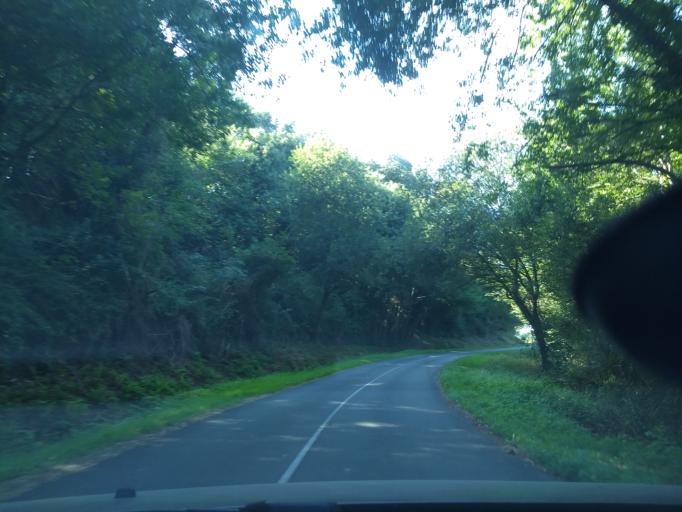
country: FR
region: Aquitaine
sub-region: Departement des Pyrenees-Atlantiques
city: Soumoulou
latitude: 43.2915
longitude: -0.1494
